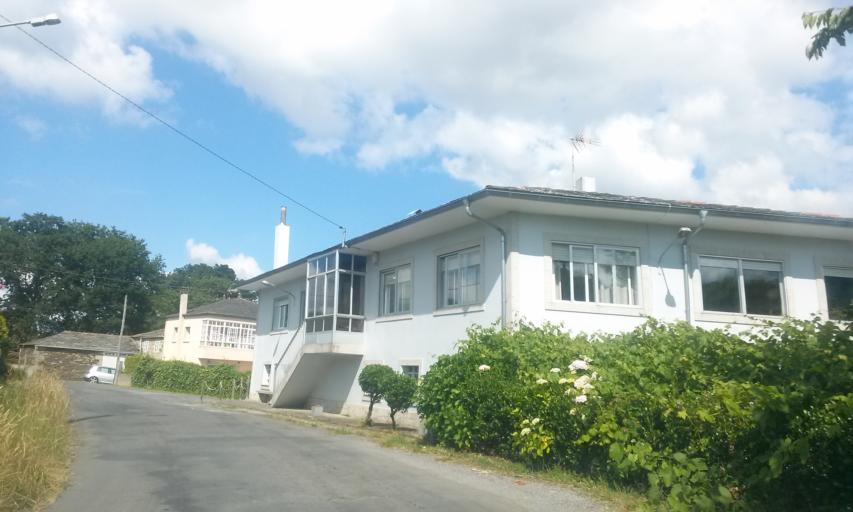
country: ES
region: Galicia
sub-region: Provincia de Lugo
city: Begonte
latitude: 43.1173
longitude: -7.6647
